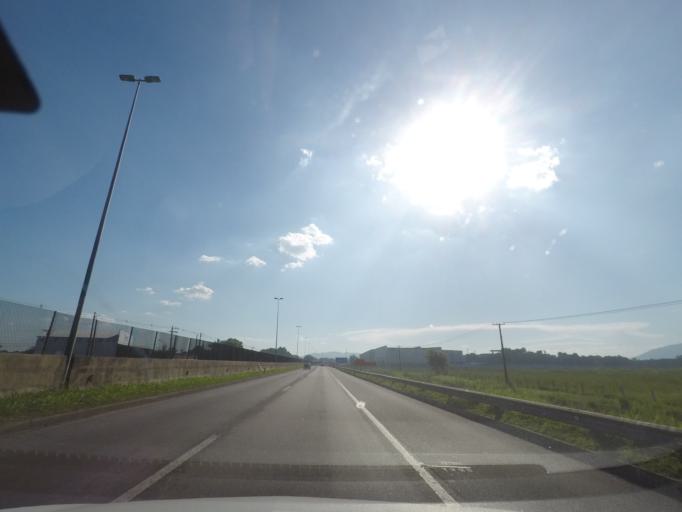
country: BR
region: Rio de Janeiro
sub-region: Duque De Caxias
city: Duque de Caxias
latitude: -22.6626
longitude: -43.2556
